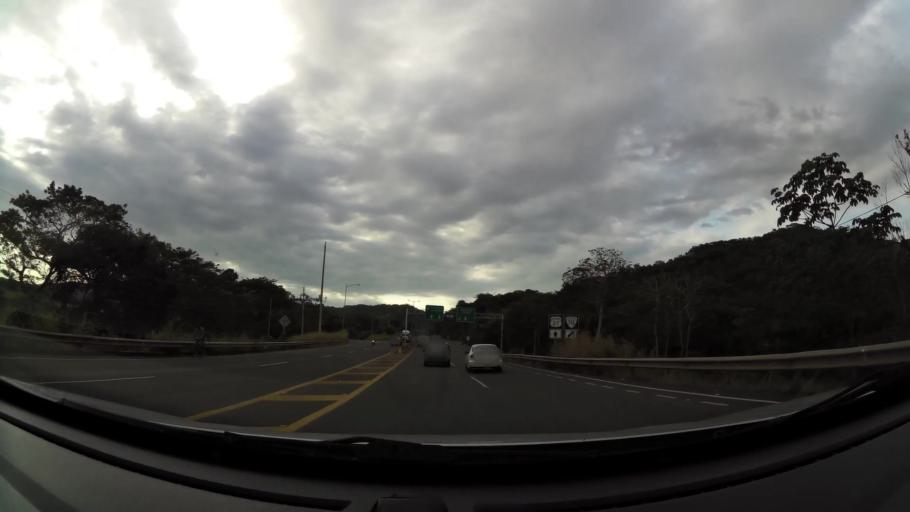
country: CR
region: Puntarenas
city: Esparza
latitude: 9.9136
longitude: -84.6738
